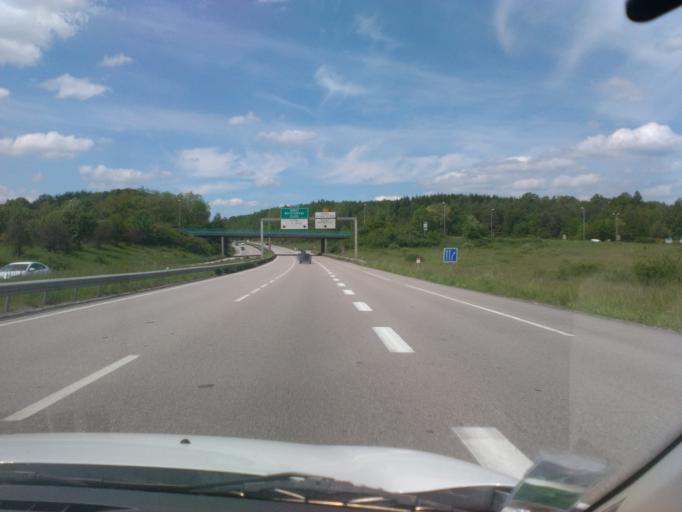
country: FR
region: Lorraine
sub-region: Departement des Vosges
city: Epinal
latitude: 48.1959
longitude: 6.4744
